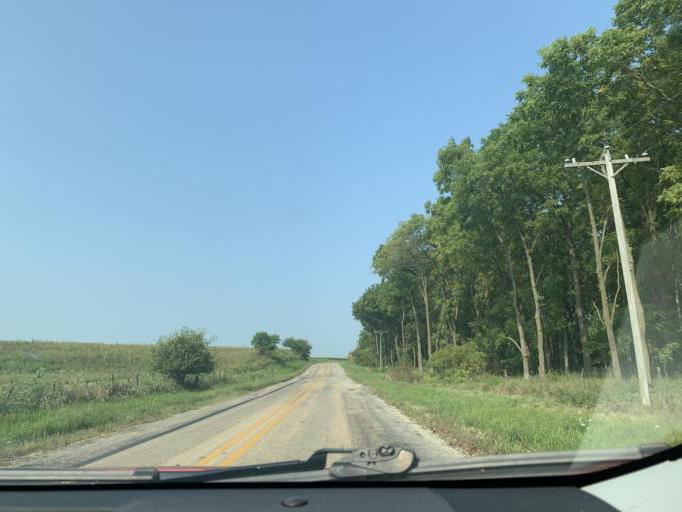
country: US
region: Illinois
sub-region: Whiteside County
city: Morrison
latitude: 41.8480
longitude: -89.8672
